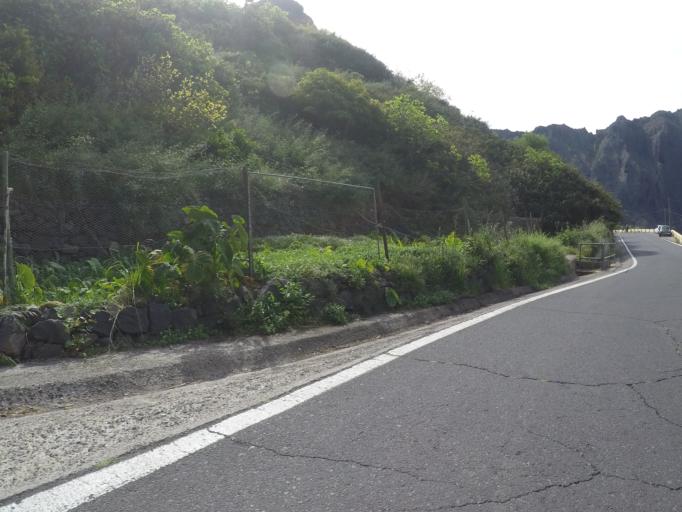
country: ES
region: Canary Islands
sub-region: Provincia de Santa Cruz de Tenerife
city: Santiago del Teide
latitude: 28.3100
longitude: -16.8415
